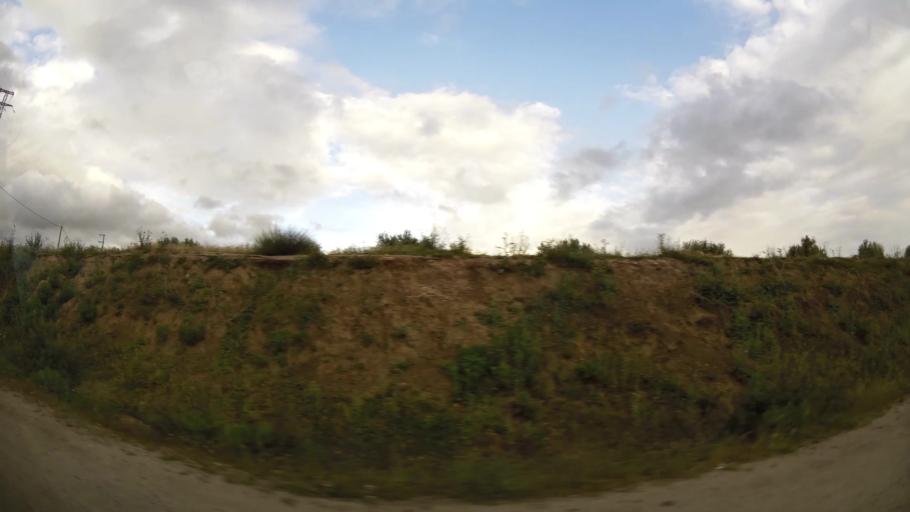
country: MA
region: Taza-Al Hoceima-Taounate
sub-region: Taza
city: Taza
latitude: 34.2595
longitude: -3.9606
